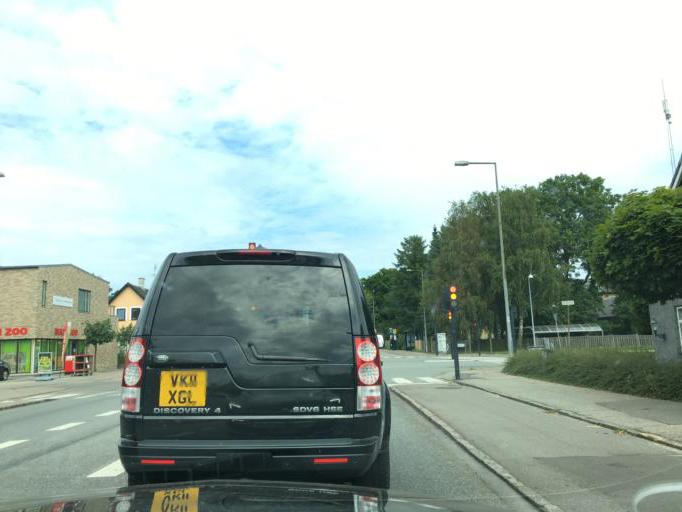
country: DK
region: Capital Region
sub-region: Horsholm Kommune
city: Horsholm
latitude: 55.8900
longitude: 12.4965
